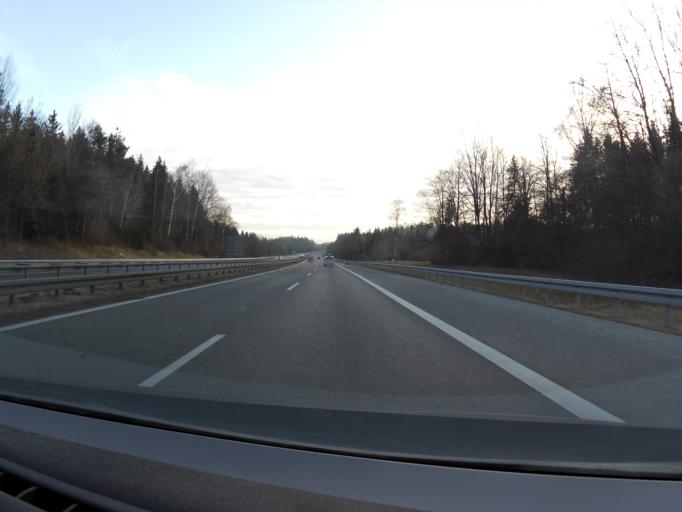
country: DE
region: Bavaria
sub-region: Upper Bavaria
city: Wolfratshausen
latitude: 47.8942
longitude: 11.3972
